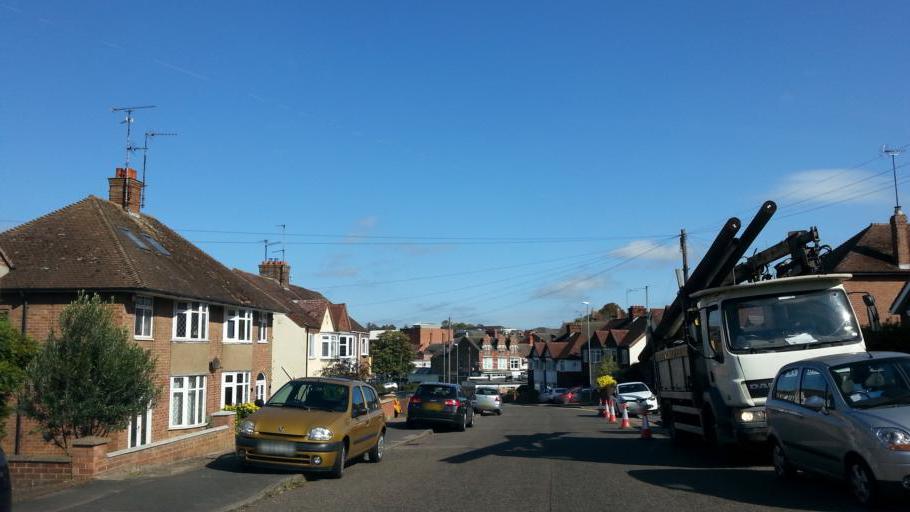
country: GB
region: England
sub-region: Northamptonshire
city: Rushden
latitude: 52.2881
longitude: -0.6013
